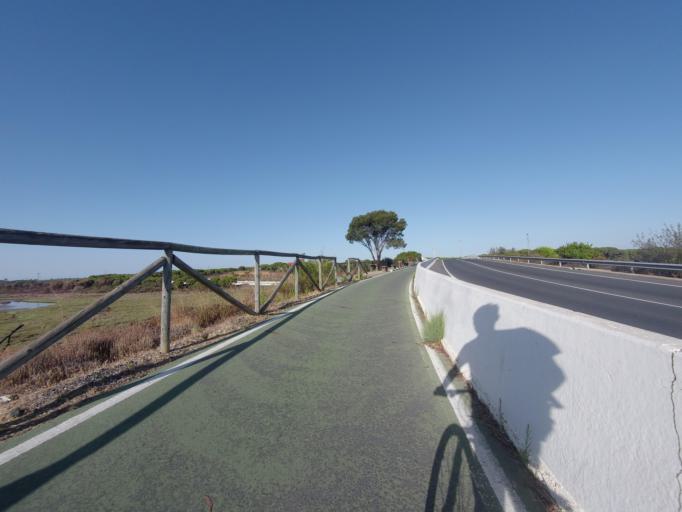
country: ES
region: Andalusia
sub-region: Provincia de Huelva
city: Aljaraque
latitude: 37.2259
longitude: -7.0220
